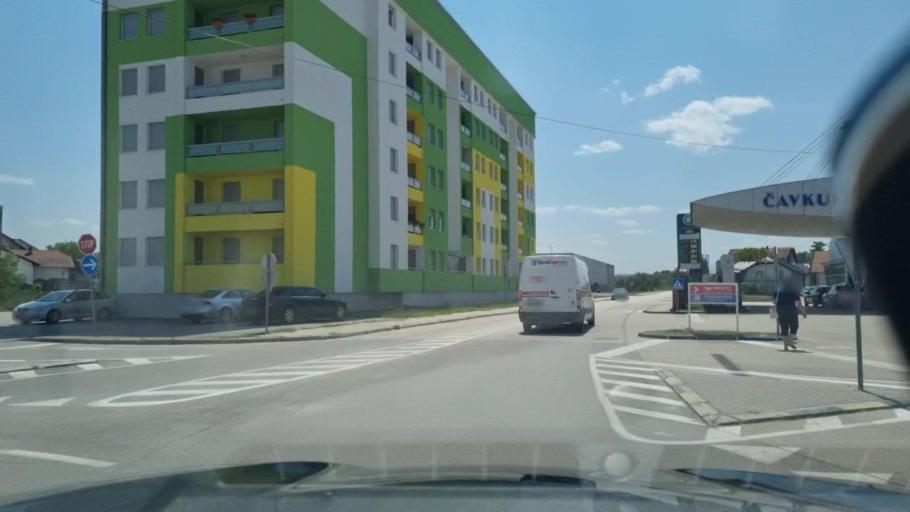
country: BA
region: Federation of Bosnia and Herzegovina
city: Sanski Most
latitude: 44.7629
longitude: 16.6730
